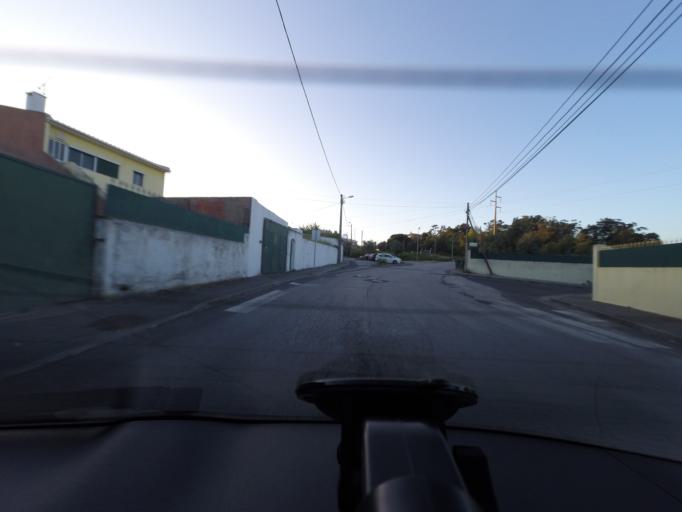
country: PT
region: Lisbon
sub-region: Sintra
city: Rio de Mouro
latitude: 38.7547
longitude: -9.3577
